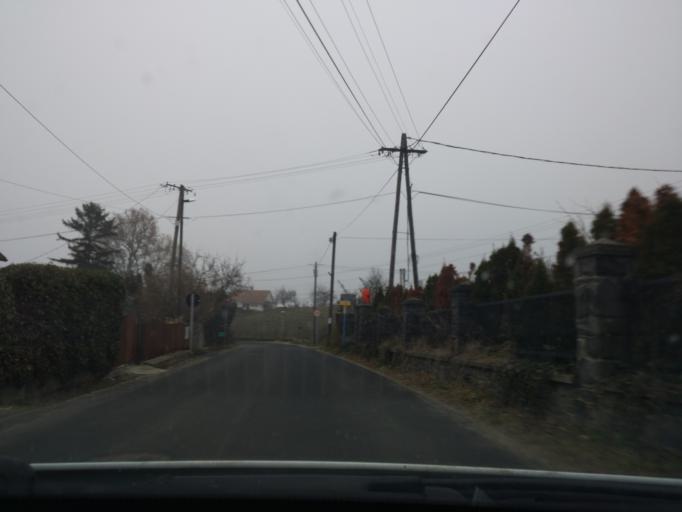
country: HU
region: Veszprem
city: Badacsonytomaj
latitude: 46.7965
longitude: 17.5101
